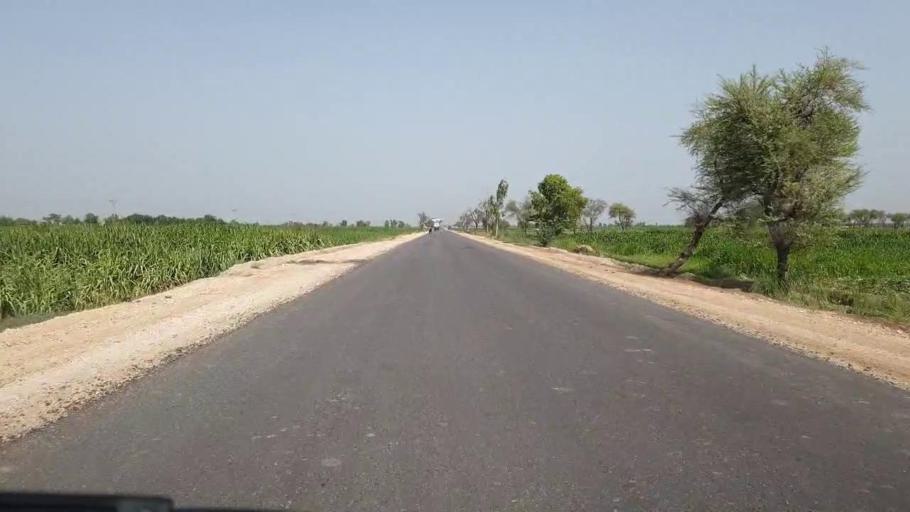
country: PK
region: Sindh
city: Sakrand
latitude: 26.2710
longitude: 68.1613
